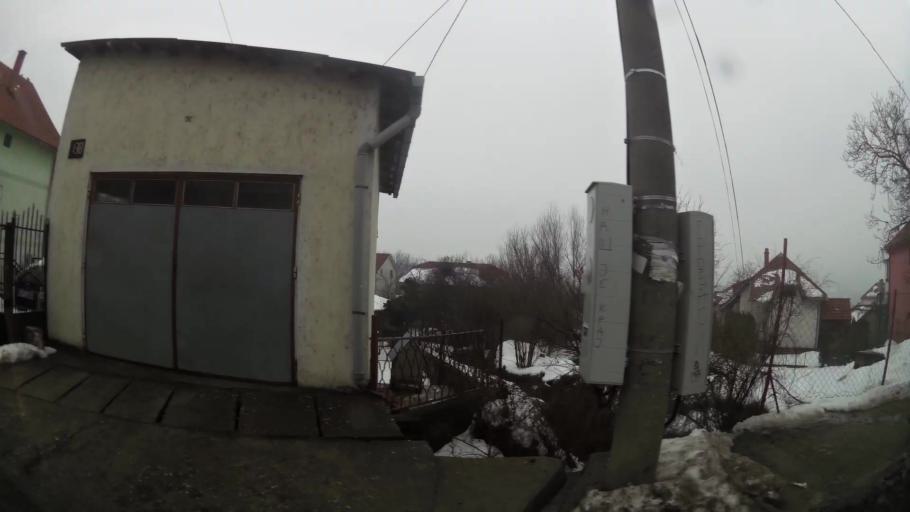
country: RS
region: Central Serbia
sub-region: Belgrade
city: Zvezdara
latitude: 44.7740
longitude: 20.5235
